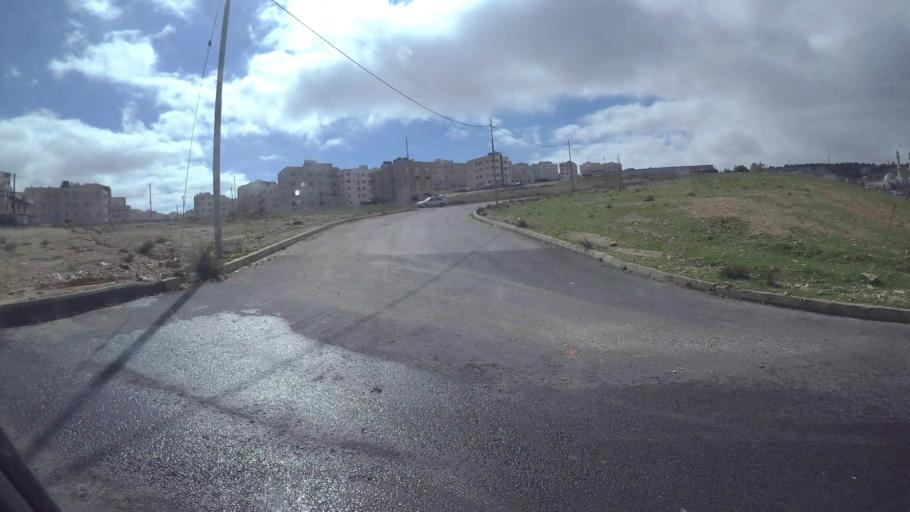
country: JO
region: Amman
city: Al Jubayhah
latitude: 32.0648
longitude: 35.8870
